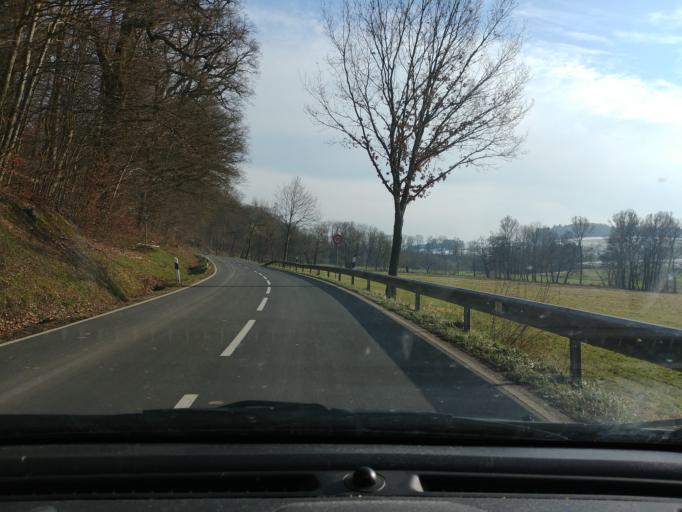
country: DE
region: Lower Saxony
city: Uslar
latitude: 51.6479
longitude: 9.6337
